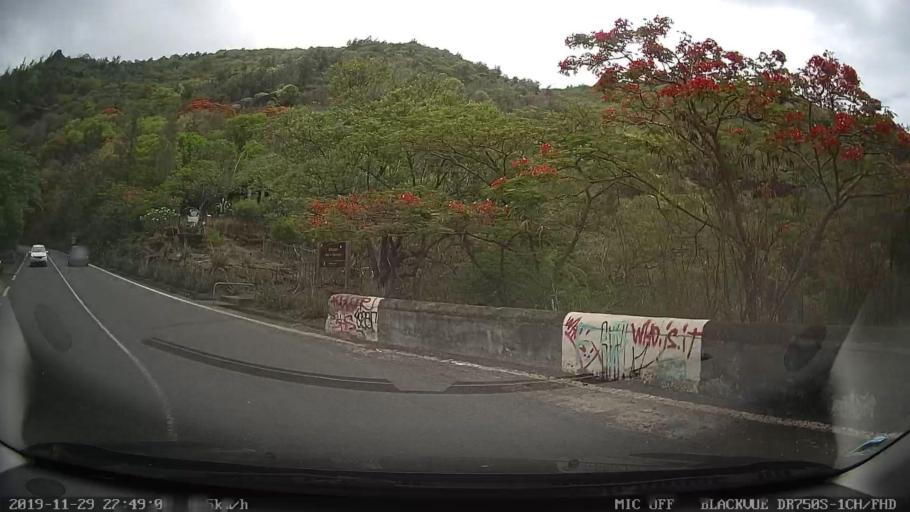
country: RE
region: Reunion
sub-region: Reunion
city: Saint-Denis
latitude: -20.8854
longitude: 55.4389
